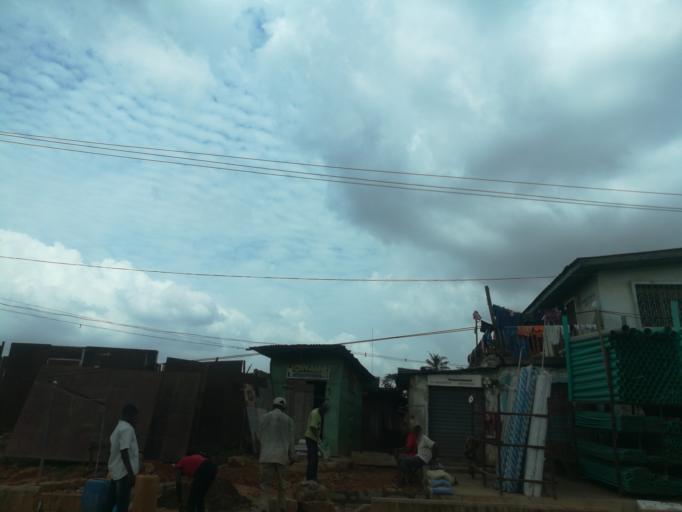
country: NG
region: Oyo
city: Ibadan
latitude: 7.4039
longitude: 3.9314
